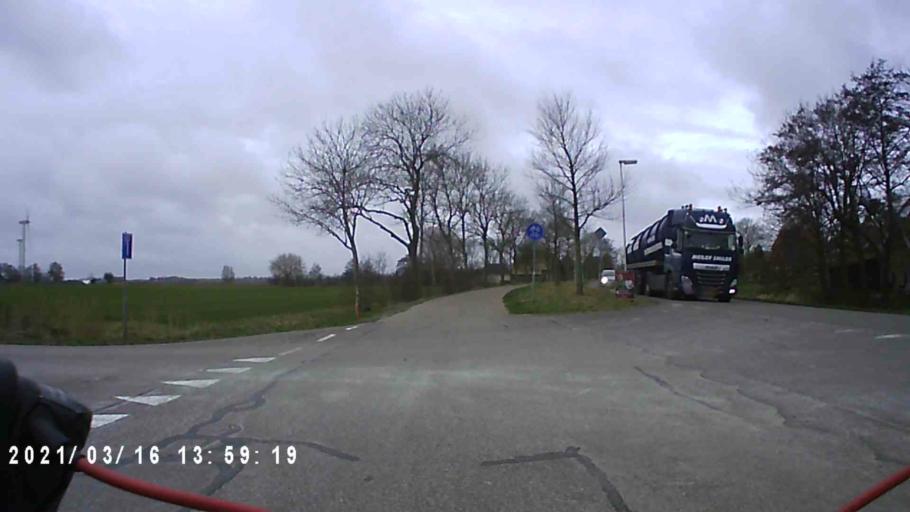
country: NL
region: Friesland
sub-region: Gemeente Franekeradeel
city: Sexbierum
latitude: 53.1837
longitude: 5.4977
